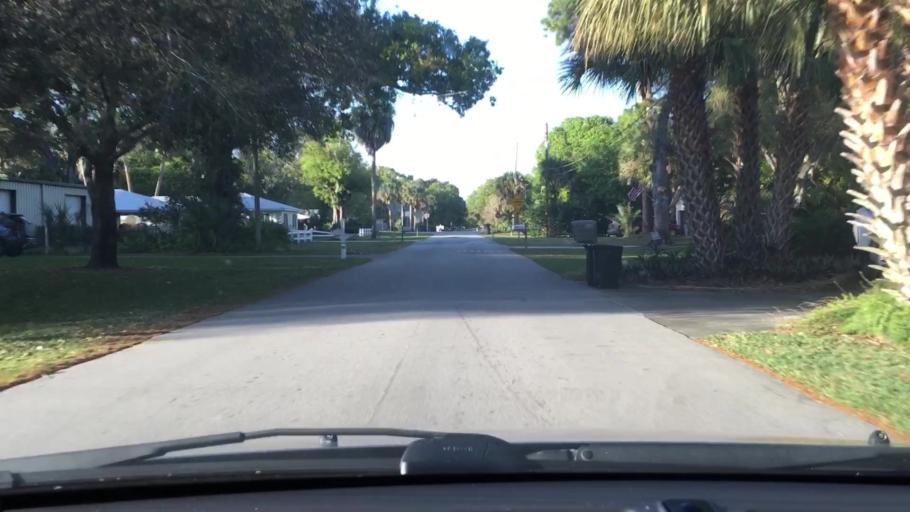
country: US
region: Florida
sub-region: Indian River County
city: Vero Beach South
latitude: 27.6449
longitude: -80.4409
